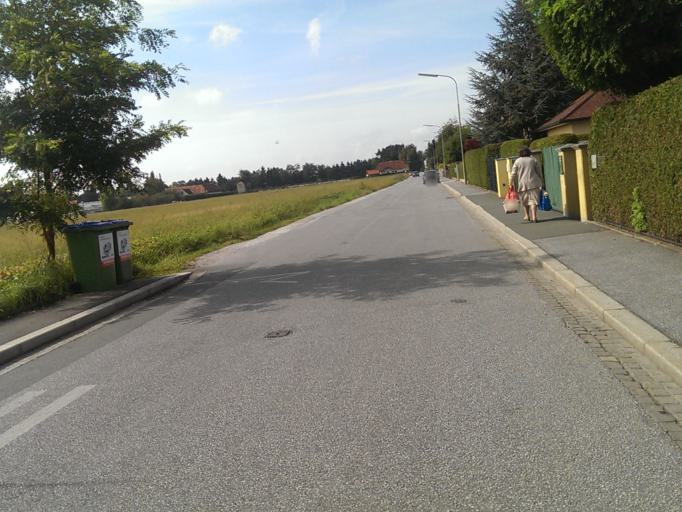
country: AT
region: Styria
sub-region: Politischer Bezirk Graz-Umgebung
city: Raaba
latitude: 47.0435
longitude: 15.4739
